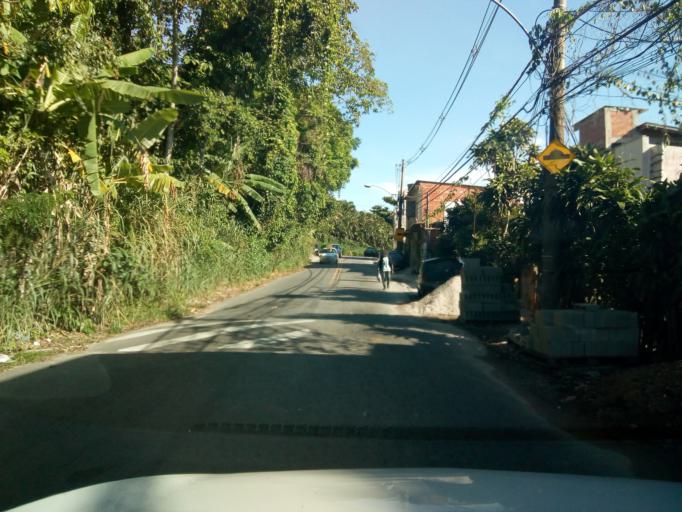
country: BR
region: Rio de Janeiro
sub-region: Nilopolis
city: Nilopolis
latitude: -23.0262
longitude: -43.5008
